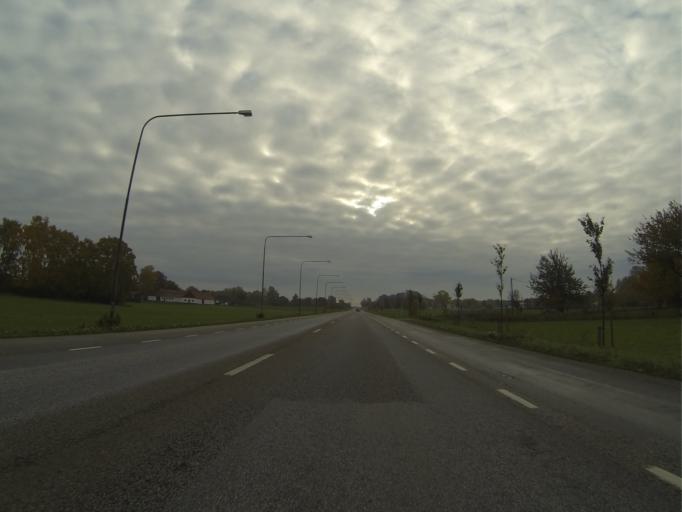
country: SE
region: Skane
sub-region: Tomelilla Kommun
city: Tomelilla
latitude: 55.5540
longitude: 13.9348
